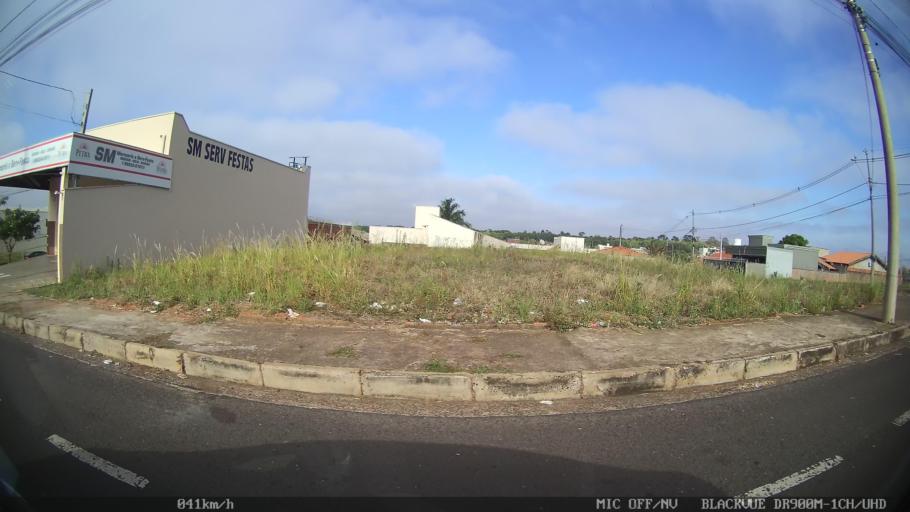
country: BR
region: Sao Paulo
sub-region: Sao Jose Do Rio Preto
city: Sao Jose do Rio Preto
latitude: -20.8015
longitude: -49.4308
